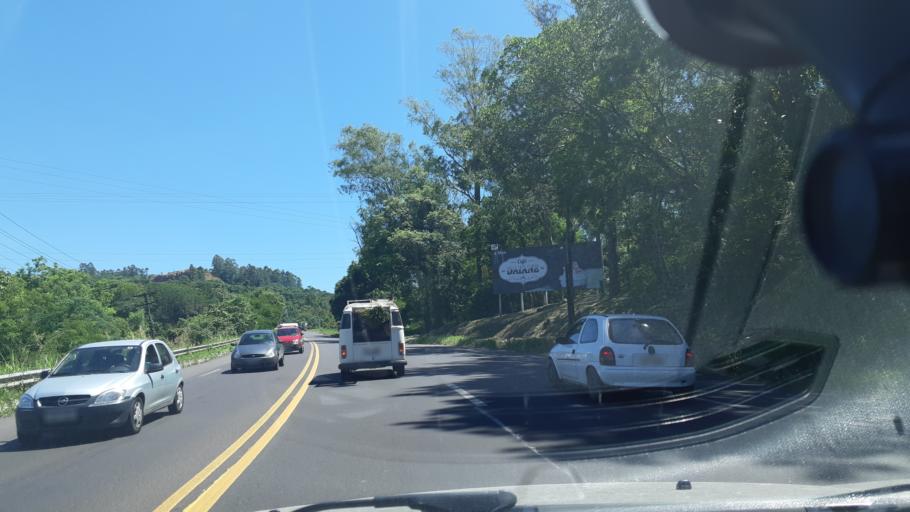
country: BR
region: Rio Grande do Sul
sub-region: Estancia Velha
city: Estancia Velha
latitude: -29.6376
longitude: -51.1419
